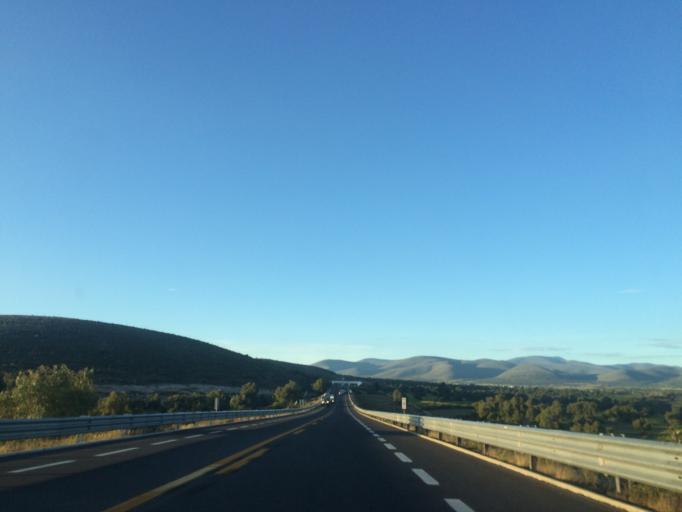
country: MX
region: Puebla
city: Cuacnopalan
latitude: 18.8013
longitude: -97.4899
